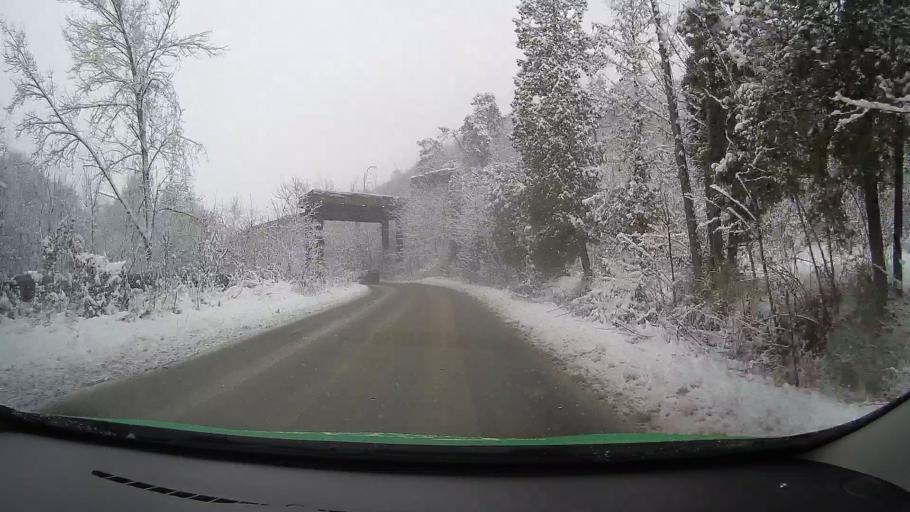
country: RO
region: Hunedoara
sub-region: Comuna Teliucu Inferior
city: Teliucu Inferior
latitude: 45.7332
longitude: 22.8809
